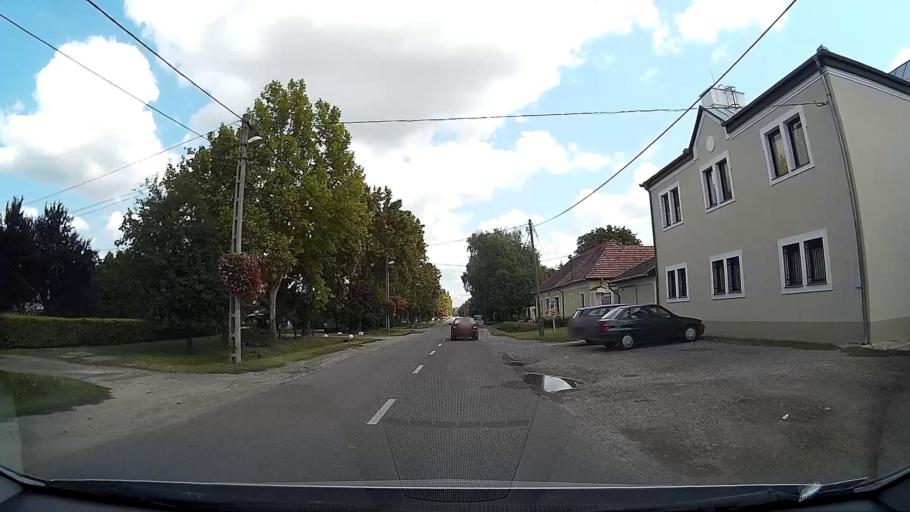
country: HU
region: Pest
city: Tahitotfalu
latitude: 47.7556
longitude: 19.0905
